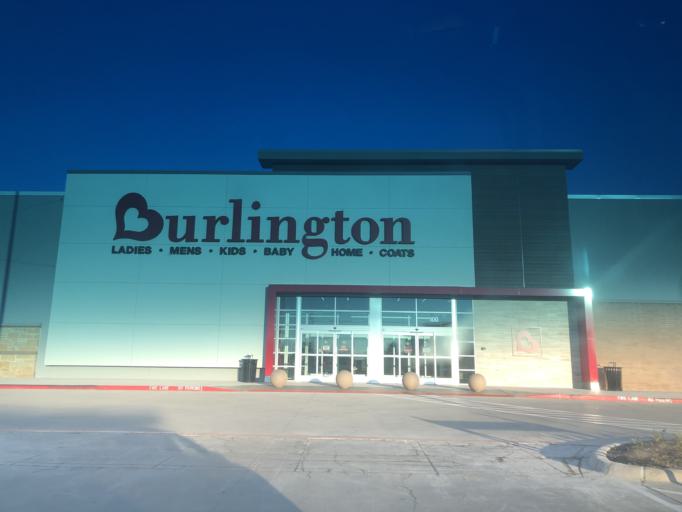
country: US
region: Texas
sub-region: Dallas County
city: Grand Prairie
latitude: 32.6953
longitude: -97.0275
